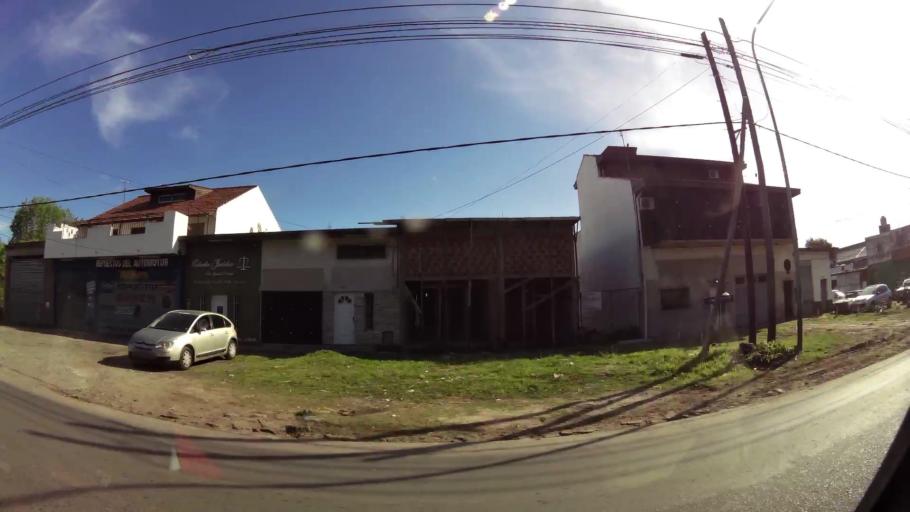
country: AR
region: Buenos Aires
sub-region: Partido de Quilmes
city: Quilmes
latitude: -34.8023
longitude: -58.2229
